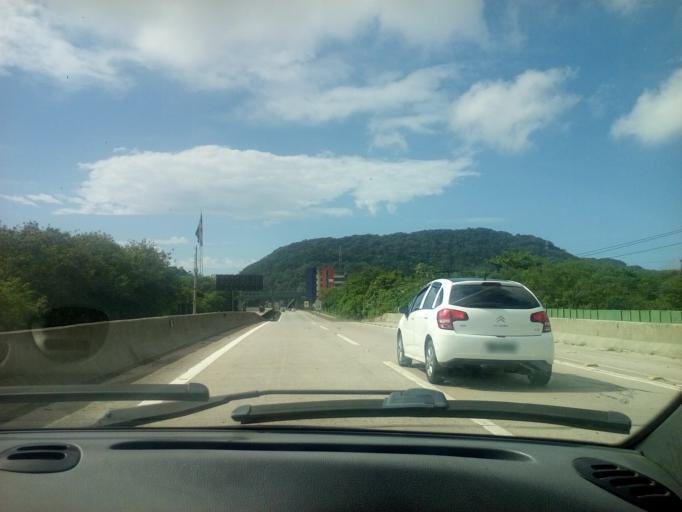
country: BR
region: Sao Paulo
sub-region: Guaruja
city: Guaruja
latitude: -23.9795
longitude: -46.2666
